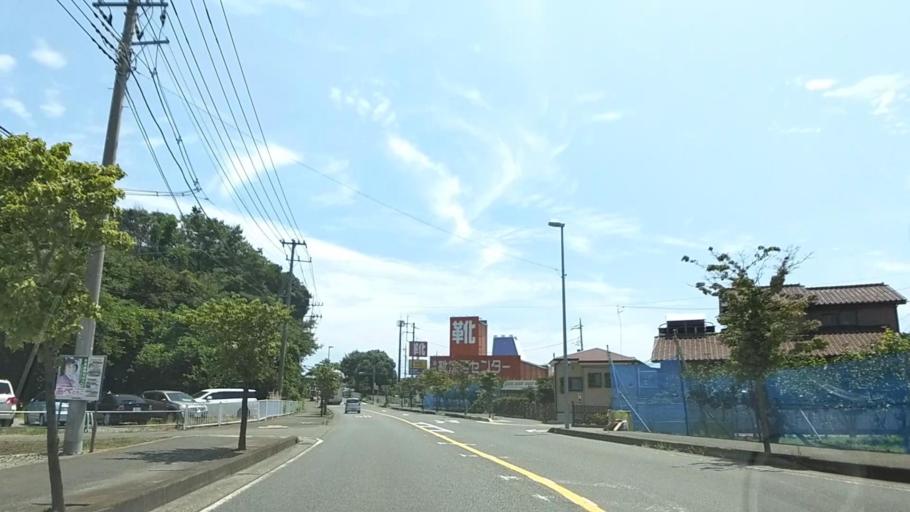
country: JP
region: Kanagawa
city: Atsugi
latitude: 35.3847
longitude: 139.3818
